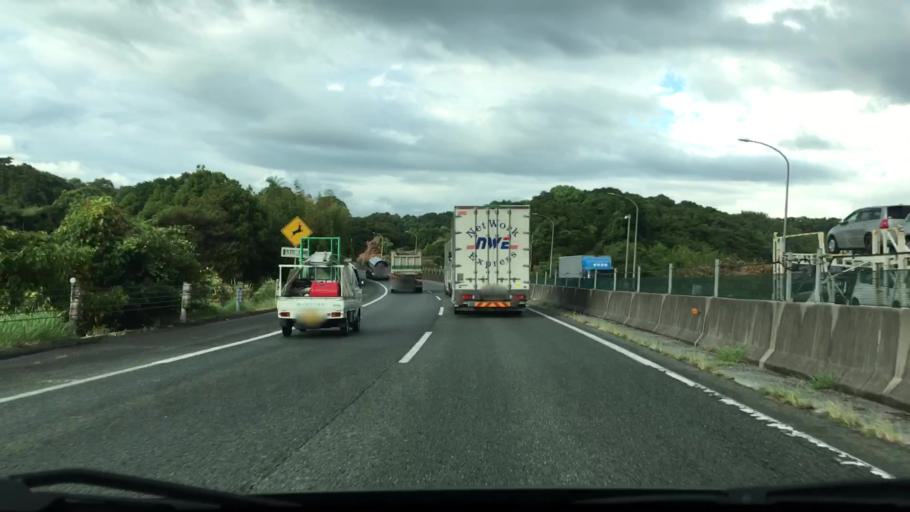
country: JP
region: Fukuoka
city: Nishifukuma
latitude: 33.7434
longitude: 130.5249
